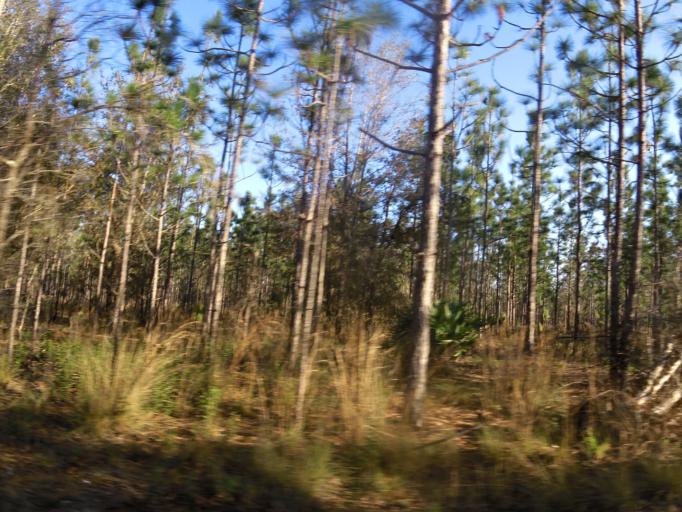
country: US
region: Florida
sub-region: Clay County
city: Middleburg
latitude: 30.1507
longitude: -81.8865
